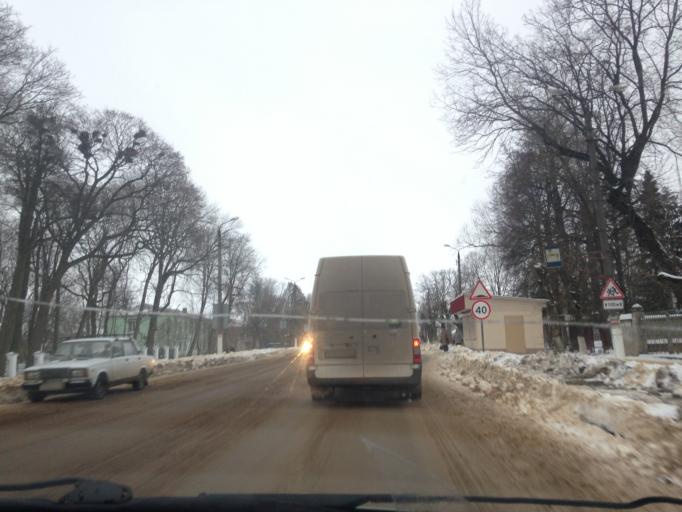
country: RU
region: Tula
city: Shchekino
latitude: 54.0014
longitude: 37.5105
